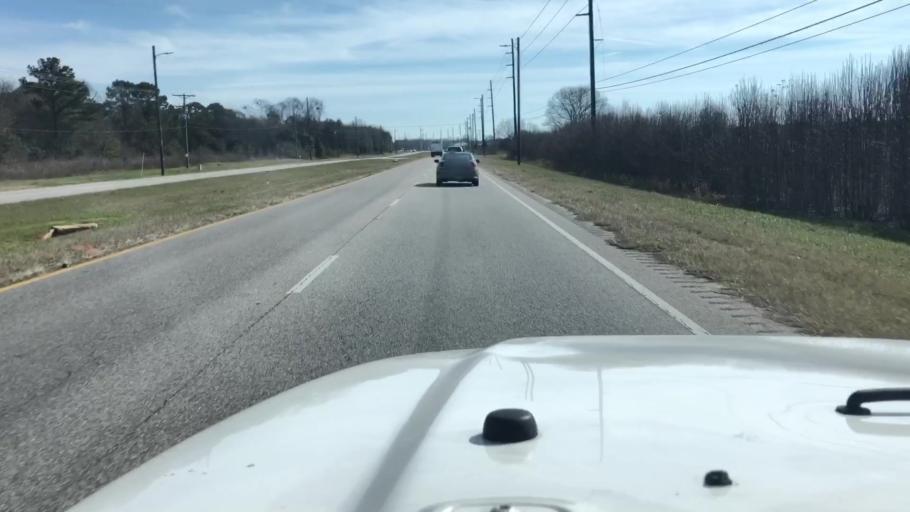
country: US
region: Alabama
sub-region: Montgomery County
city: Pike Road
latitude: 32.3764
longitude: -86.1521
